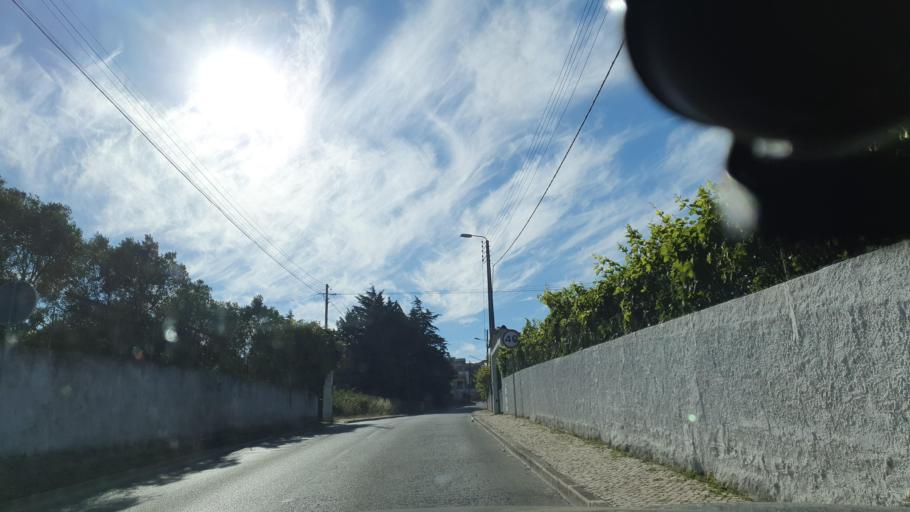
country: PT
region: Lisbon
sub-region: Sintra
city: Belas
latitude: 38.7954
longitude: -9.2508
